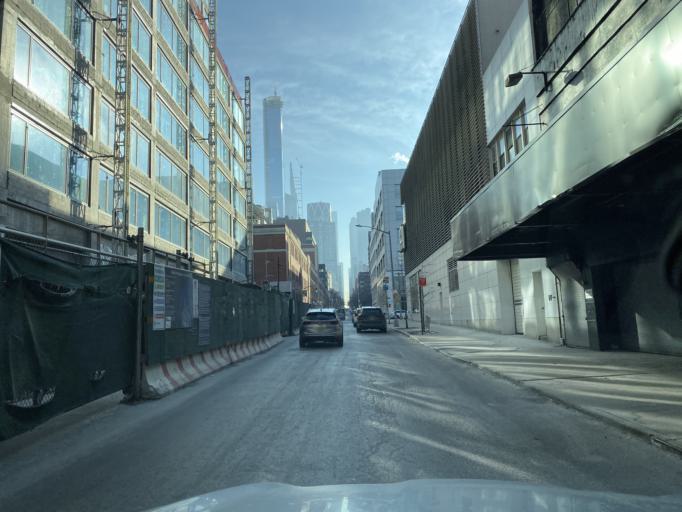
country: US
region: New Jersey
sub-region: Hudson County
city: Guttenberg
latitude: 40.7700
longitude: -73.9928
